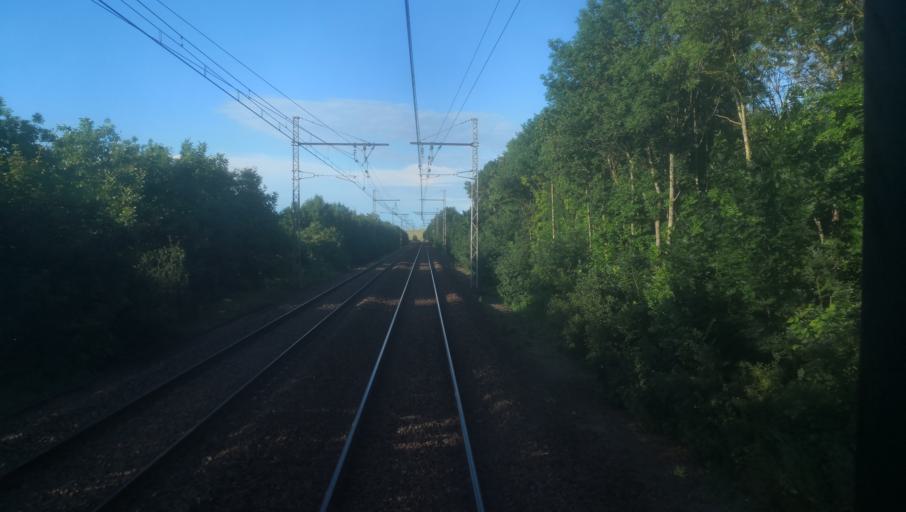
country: FR
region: Centre
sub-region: Departement de l'Indre
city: Sainte-Lizaigne
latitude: 46.9830
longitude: 2.0134
